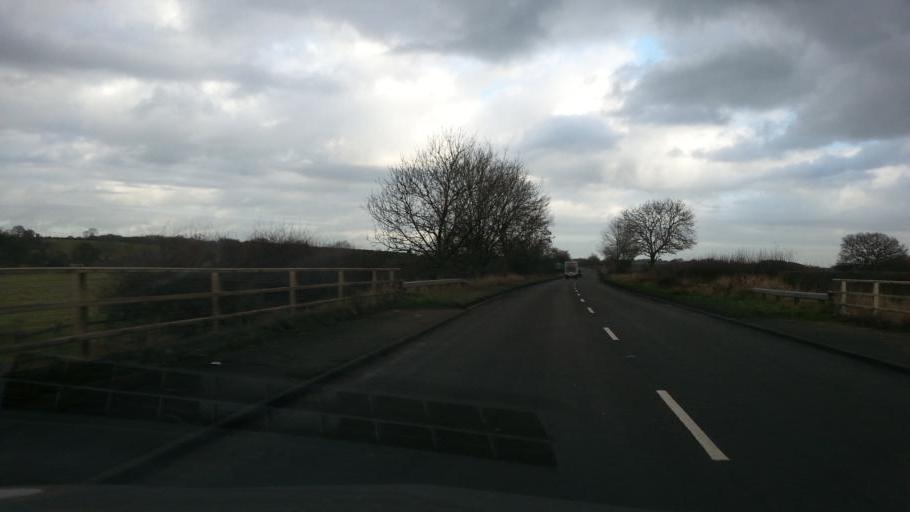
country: GB
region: England
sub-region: Staffordshire
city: Alrewas
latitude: 52.7548
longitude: -1.8129
